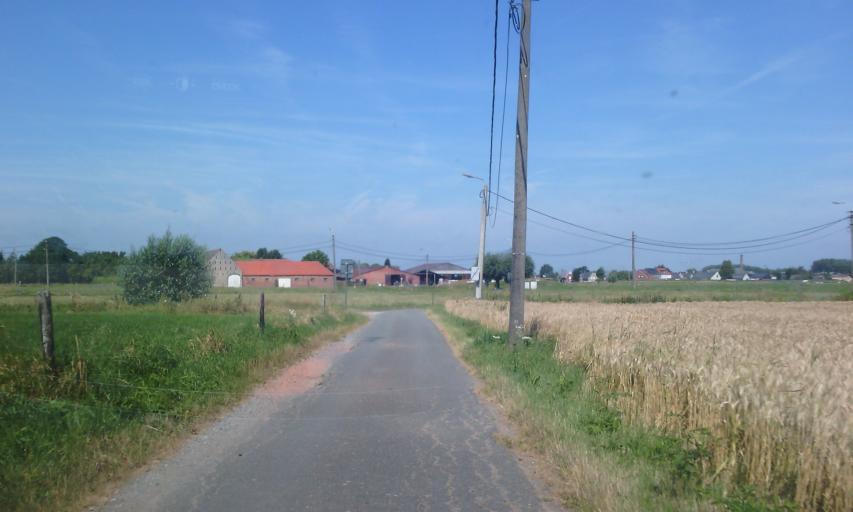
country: BE
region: Flanders
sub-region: Provincie Oost-Vlaanderen
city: Wichelen
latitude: 50.9967
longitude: 3.9975
